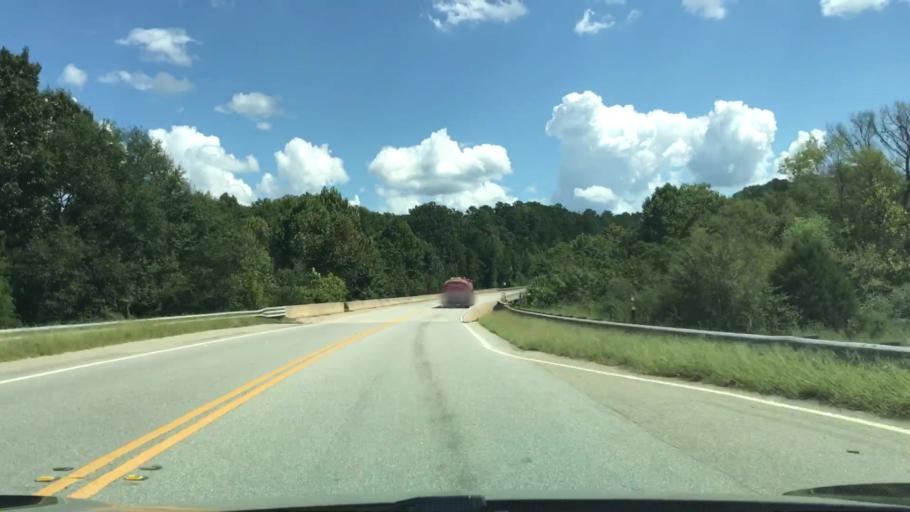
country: US
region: Georgia
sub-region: Oconee County
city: Watkinsville
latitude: 33.7212
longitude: -83.2964
